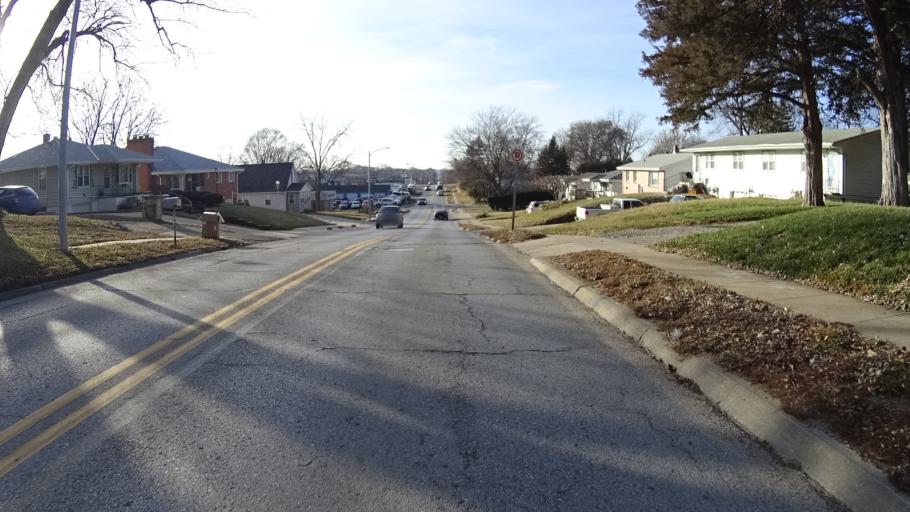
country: US
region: Nebraska
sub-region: Sarpy County
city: La Vista
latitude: 41.1909
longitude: -95.9707
